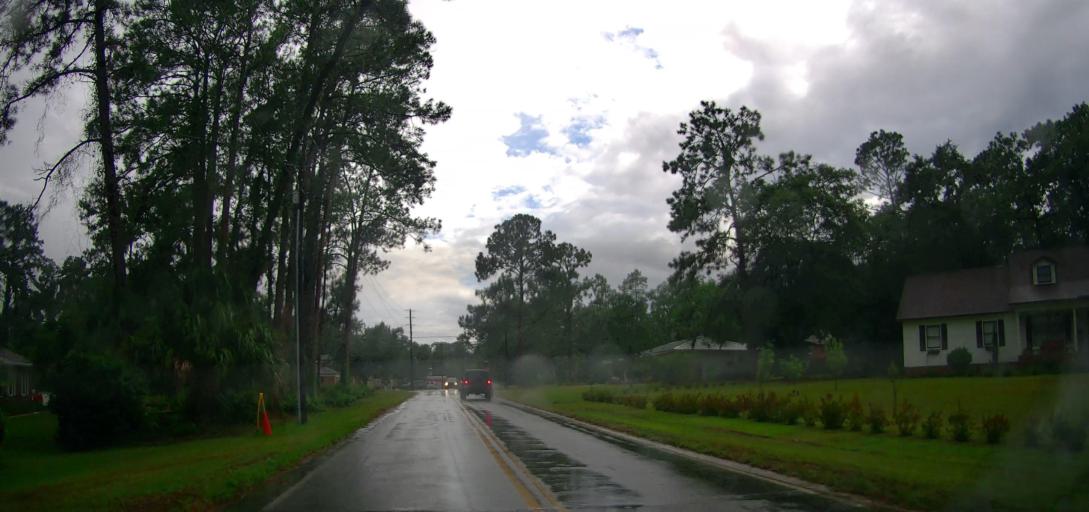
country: US
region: Georgia
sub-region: Ware County
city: Sunnyside
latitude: 31.2228
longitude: -82.3284
